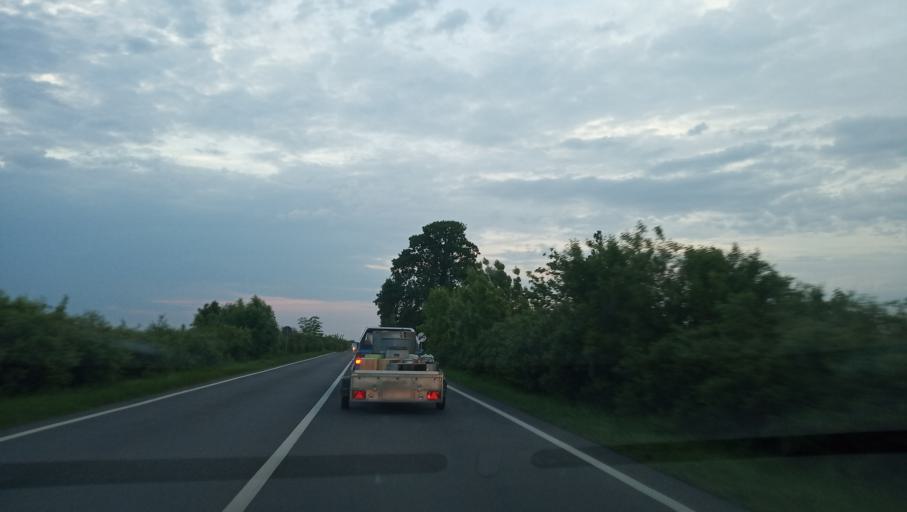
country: RO
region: Timis
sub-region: Comuna Voiteg
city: Voiteg
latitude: 45.5064
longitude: 21.2385
